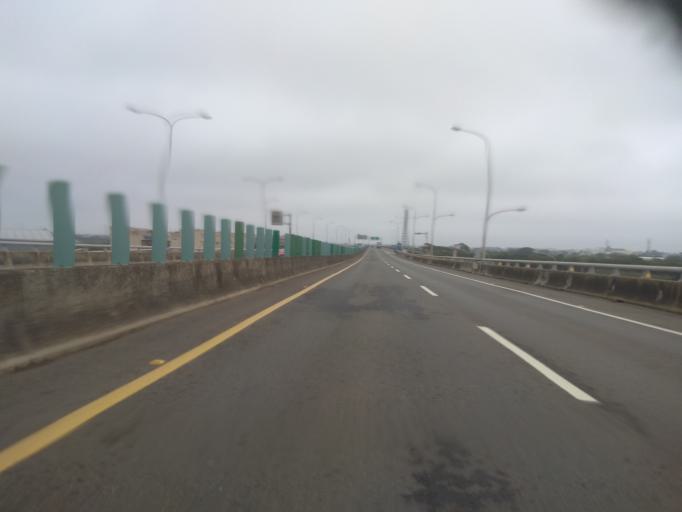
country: TW
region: Taiwan
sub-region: Hsinchu
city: Zhubei
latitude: 24.9997
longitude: 121.1014
